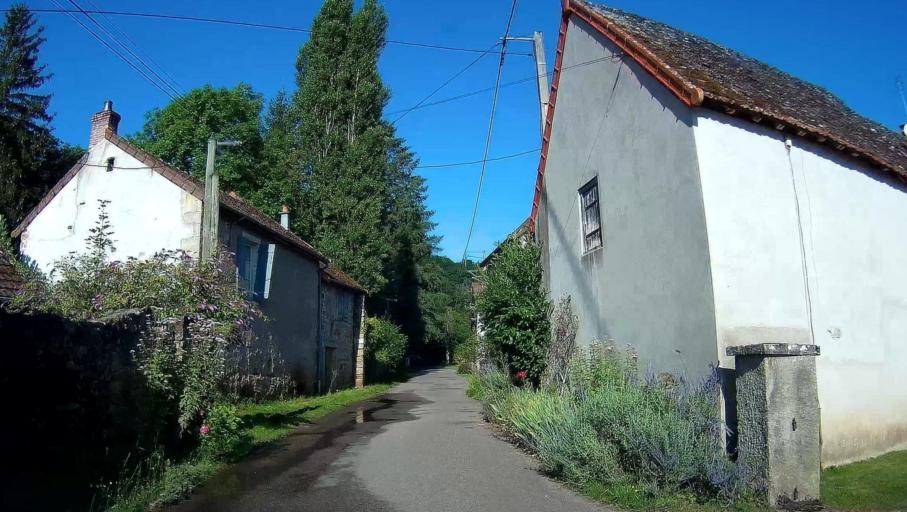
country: FR
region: Bourgogne
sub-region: Departement de Saone-et-Loire
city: Couches
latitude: 46.8638
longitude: 4.5921
